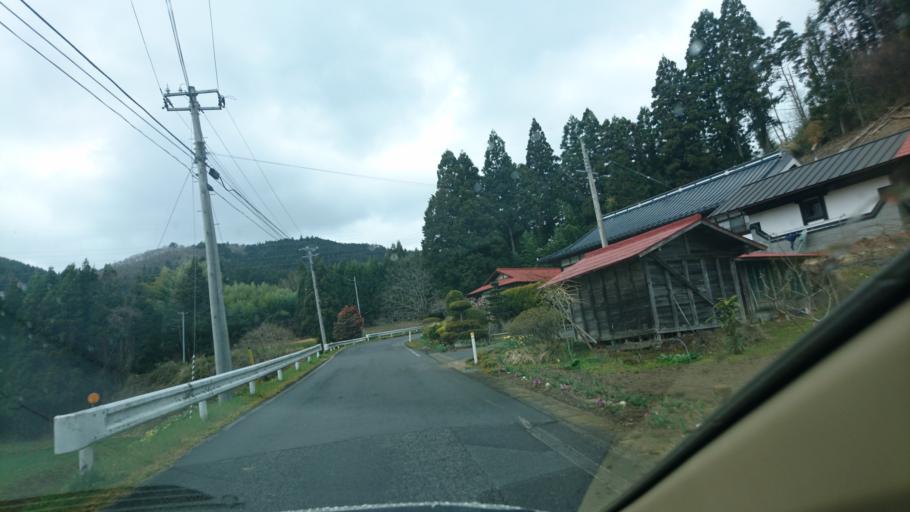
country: JP
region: Iwate
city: Ichinoseki
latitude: 38.9438
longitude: 141.3056
